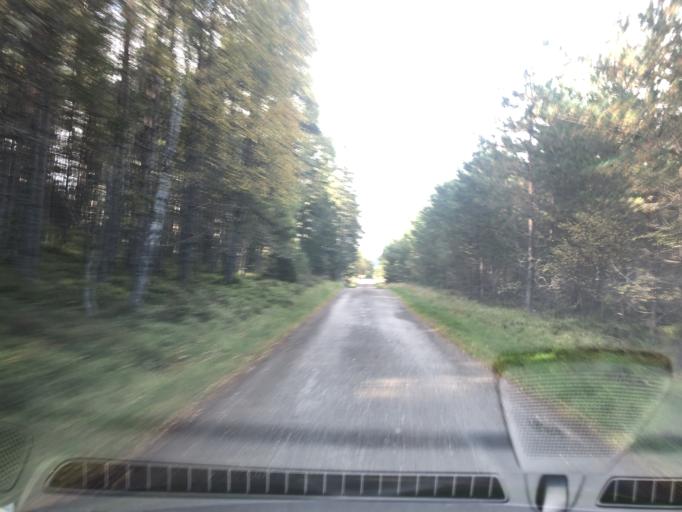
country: GB
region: Scotland
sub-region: Highland
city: Aviemore
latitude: 57.1133
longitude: -3.8926
